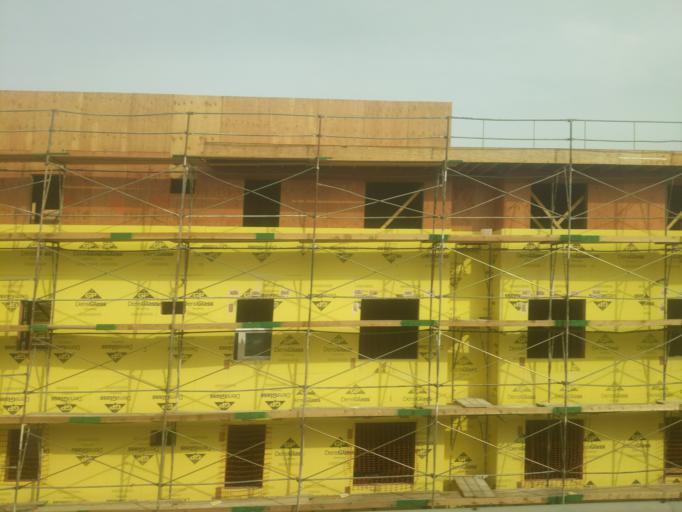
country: US
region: California
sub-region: Alameda County
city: Alameda
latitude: 37.7739
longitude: -122.2225
